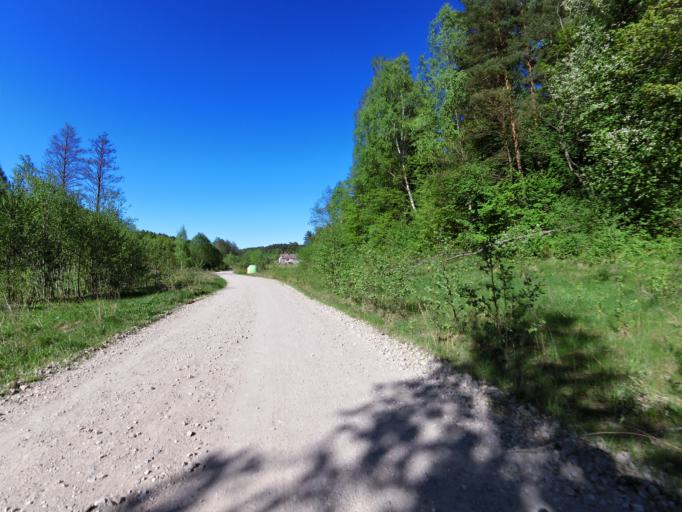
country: LT
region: Vilnius County
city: Pilaite
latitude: 54.6835
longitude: 25.1834
